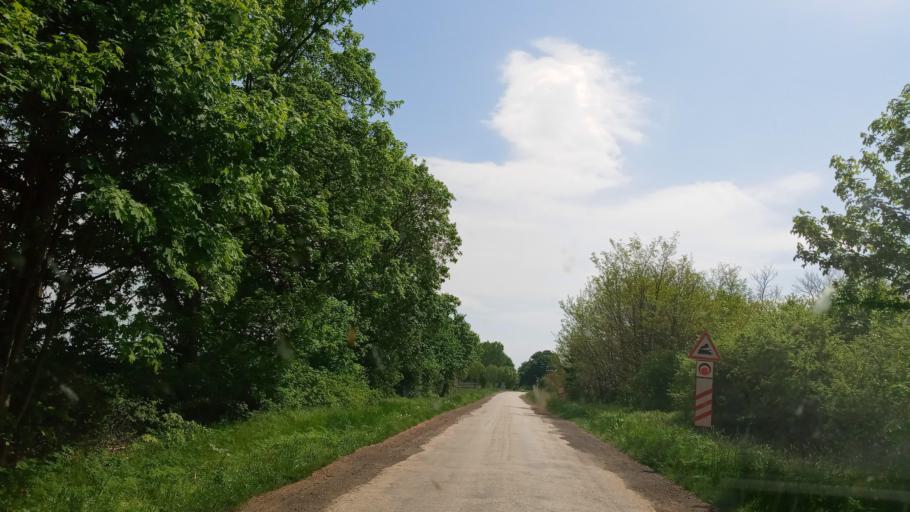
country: HU
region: Baranya
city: Villany
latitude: 45.8300
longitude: 18.5014
